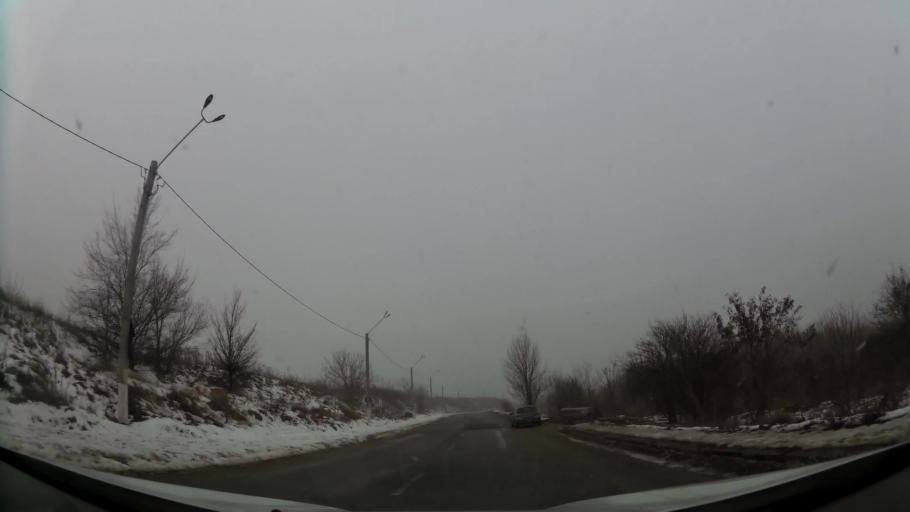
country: RO
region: Ilfov
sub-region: Comuna Chiajna
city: Rosu
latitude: 44.4595
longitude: 25.9942
